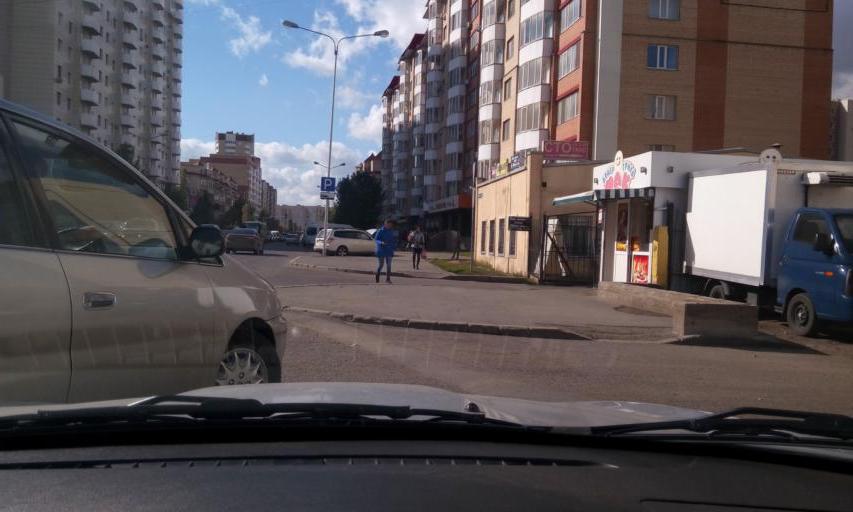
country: KZ
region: Astana Qalasy
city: Astana
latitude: 51.1692
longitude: 71.4070
